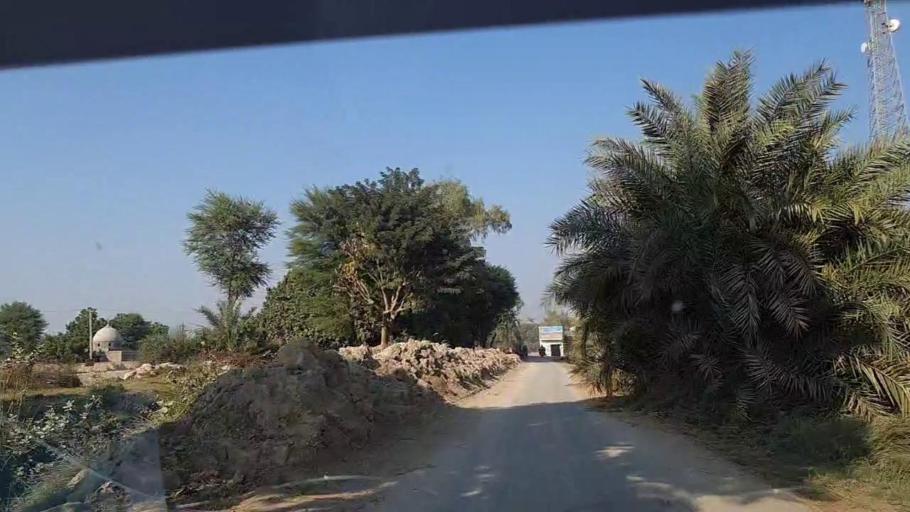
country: PK
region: Sindh
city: Sobhadero
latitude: 27.2528
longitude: 68.3290
